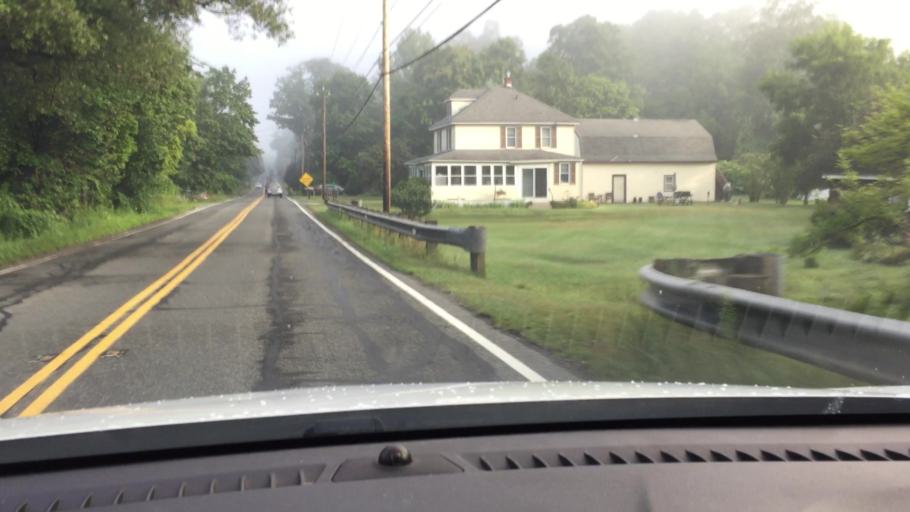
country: US
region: Massachusetts
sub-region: Berkshire County
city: Lee
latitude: 42.3268
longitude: -73.2408
